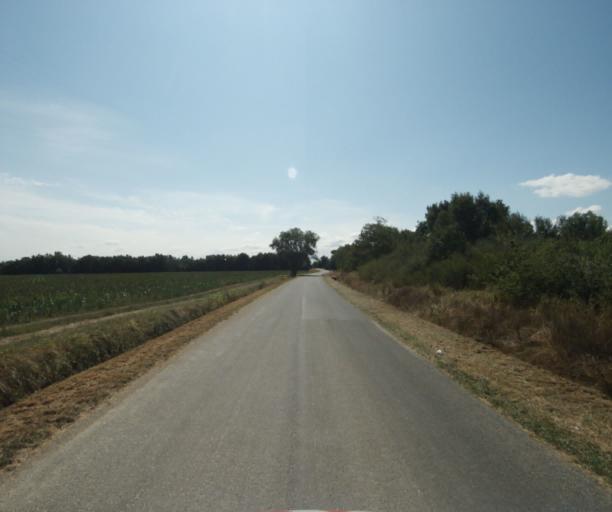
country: FR
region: Midi-Pyrenees
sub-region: Departement de la Haute-Garonne
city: Revel
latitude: 43.4783
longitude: 2.0055
